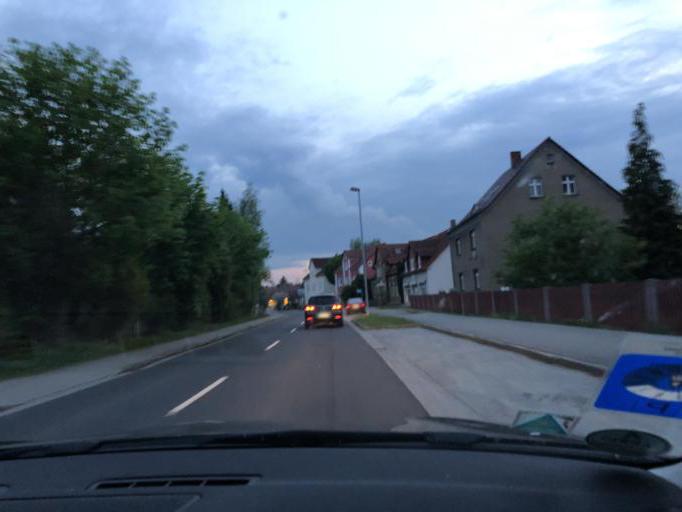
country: DE
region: Saxony
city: Krauschwitz
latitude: 51.5178
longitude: 14.7194
